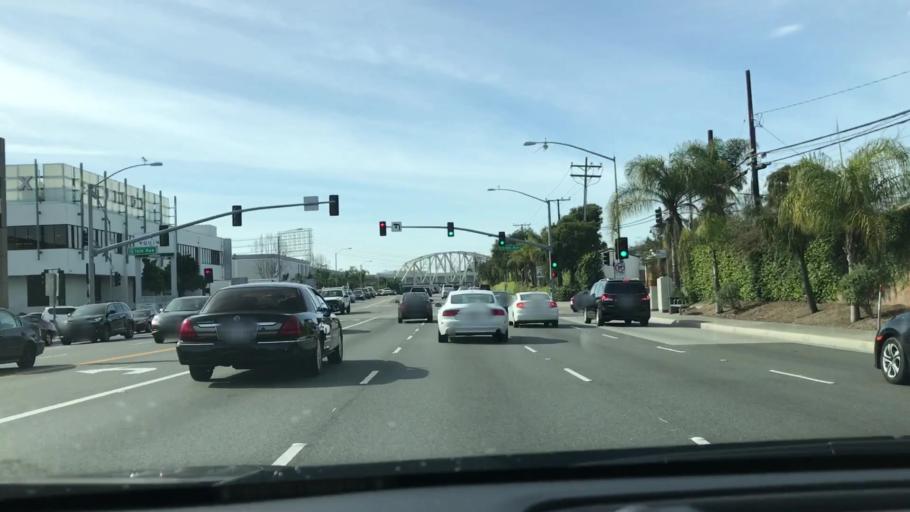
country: US
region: California
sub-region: Los Angeles County
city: Del Aire
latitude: 33.9019
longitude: -118.3737
